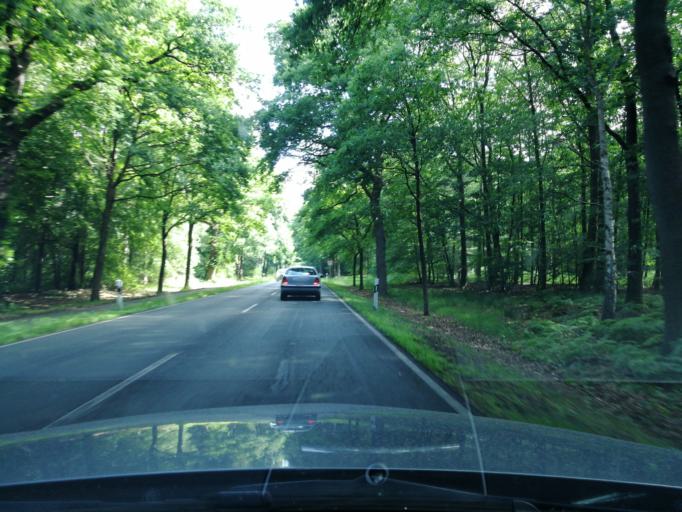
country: DE
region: North Rhine-Westphalia
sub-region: Regierungsbezirk Dusseldorf
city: Kranenburg
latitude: 51.7284
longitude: 6.0658
